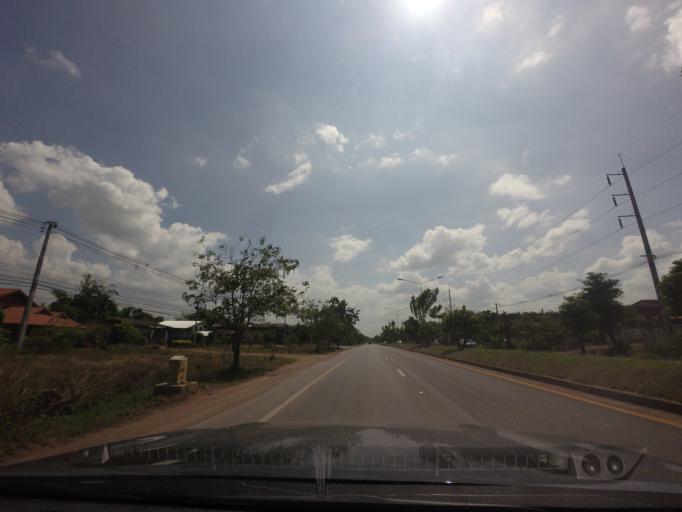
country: TH
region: Phetchabun
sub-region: Amphoe Bueng Sam Phan
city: Bueng Sam Phan
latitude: 15.8793
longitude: 101.0178
